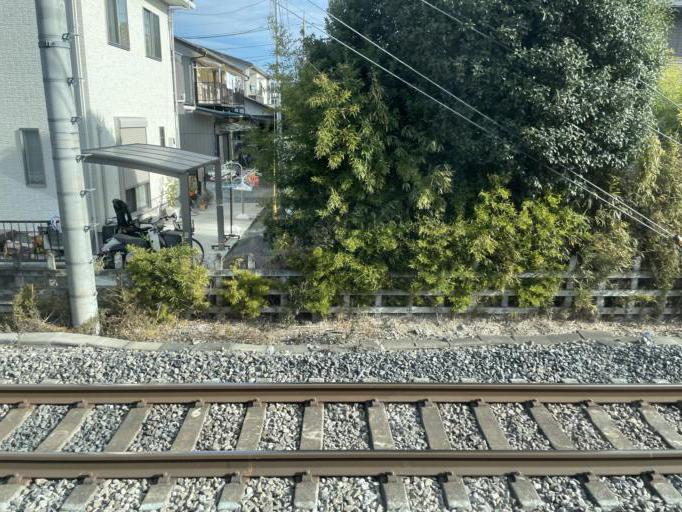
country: JP
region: Saitama
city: Okegawa
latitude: 36.0021
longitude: 139.5604
